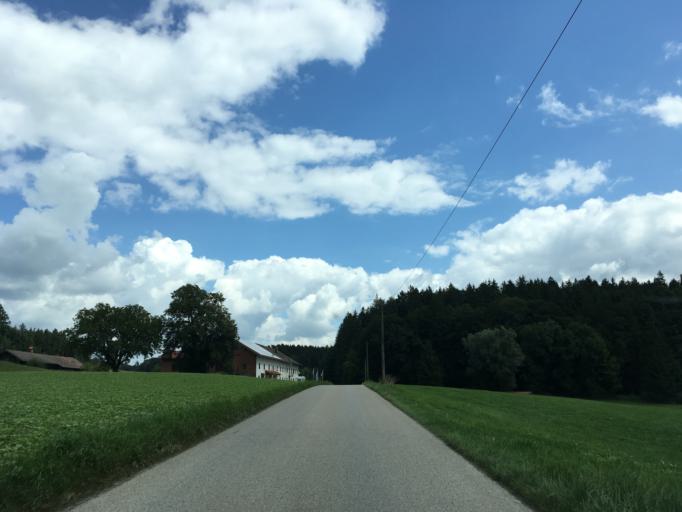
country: DE
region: Bavaria
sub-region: Upper Bavaria
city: Schnaitsee
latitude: 48.0573
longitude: 12.3327
